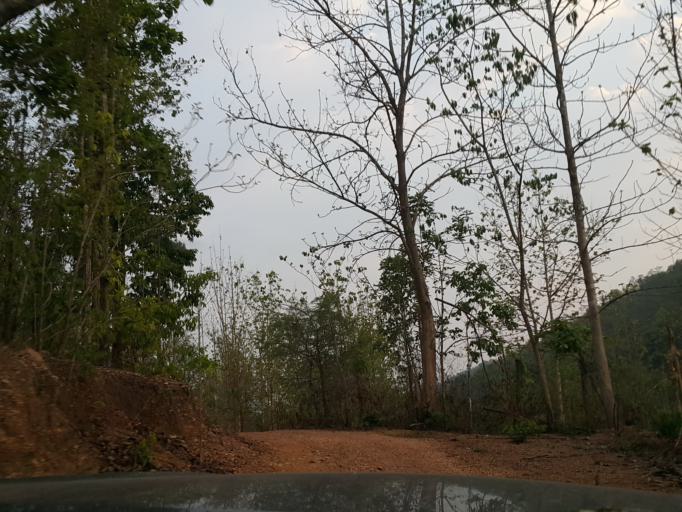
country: TH
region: Lamphun
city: Thung Hua Chang
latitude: 17.9016
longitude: 99.0815
